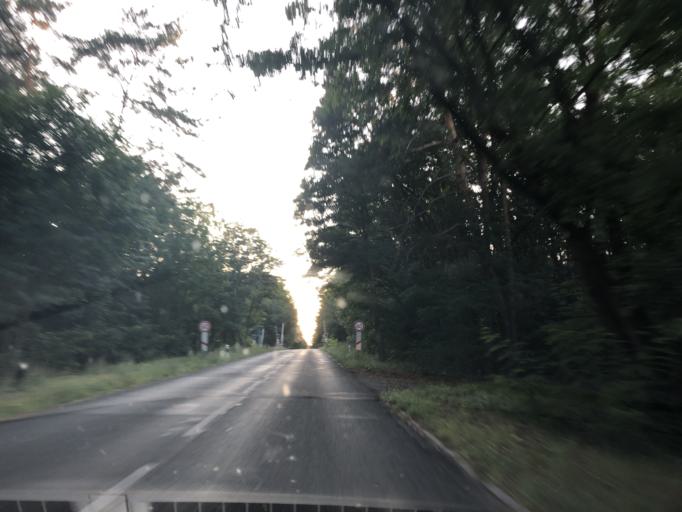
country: DE
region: Brandenburg
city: Mullrose
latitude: 52.2501
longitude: 14.4409
